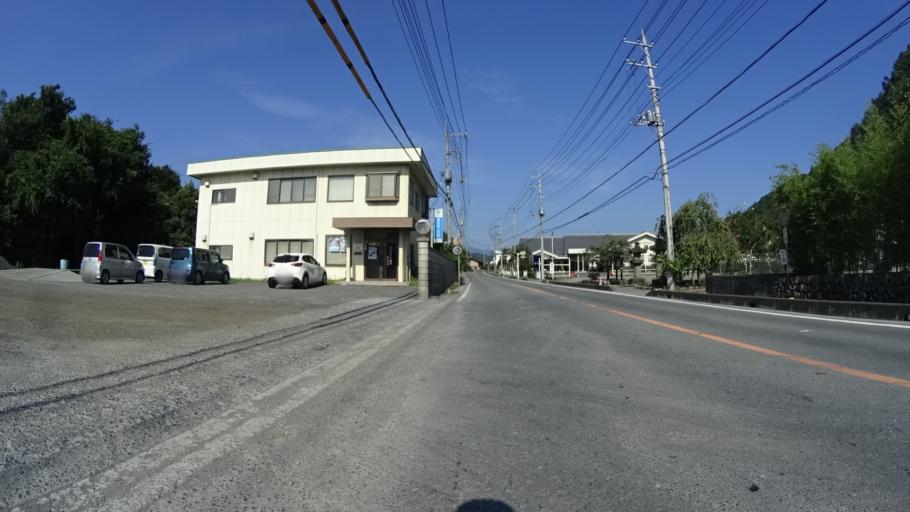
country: JP
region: Saitama
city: Chichibu
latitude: 36.0122
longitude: 139.0254
